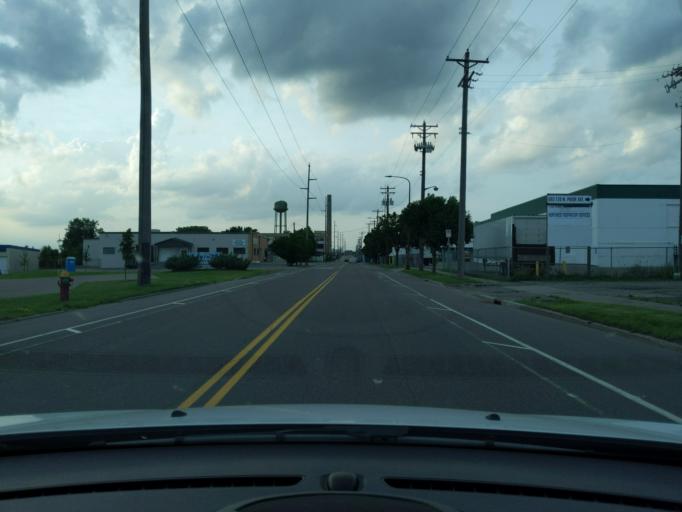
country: US
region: Minnesota
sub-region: Ramsey County
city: Falcon Heights
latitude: 44.9611
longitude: -93.1822
